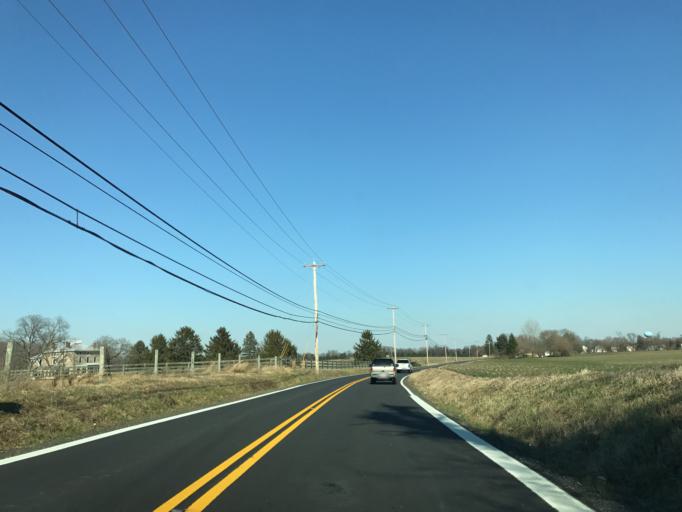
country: US
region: Maryland
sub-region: Queen Anne's County
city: Centreville
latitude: 39.0309
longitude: -76.0857
